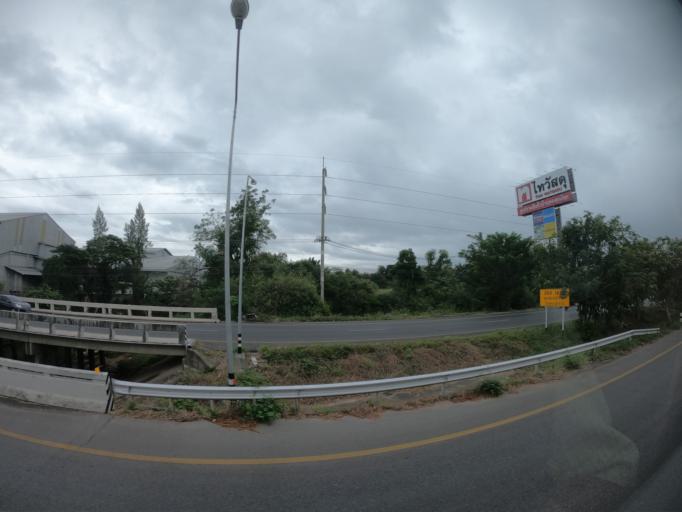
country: TH
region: Roi Et
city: Roi Et
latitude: 16.0574
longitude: 103.6197
